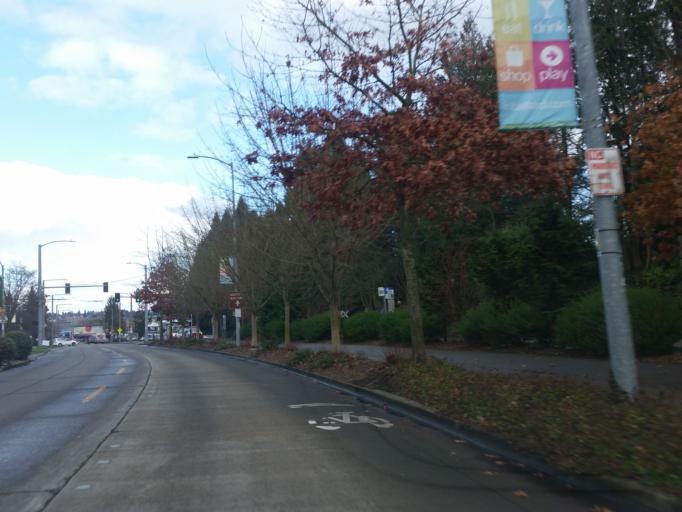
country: US
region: Washington
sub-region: King County
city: Seattle
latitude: 47.6675
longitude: -122.3996
